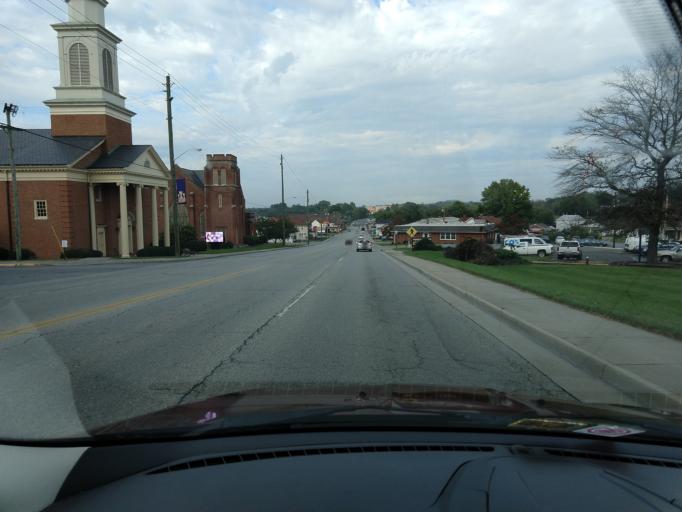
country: US
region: Virginia
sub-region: Roanoke County
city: Vinton
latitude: 37.2809
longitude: -79.8947
